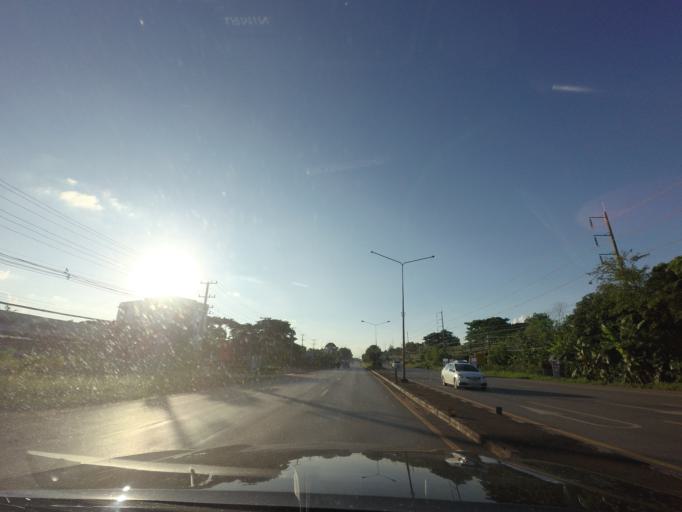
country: TH
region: Changwat Udon Thani
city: Udon Thani
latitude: 17.3791
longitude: 102.8409
